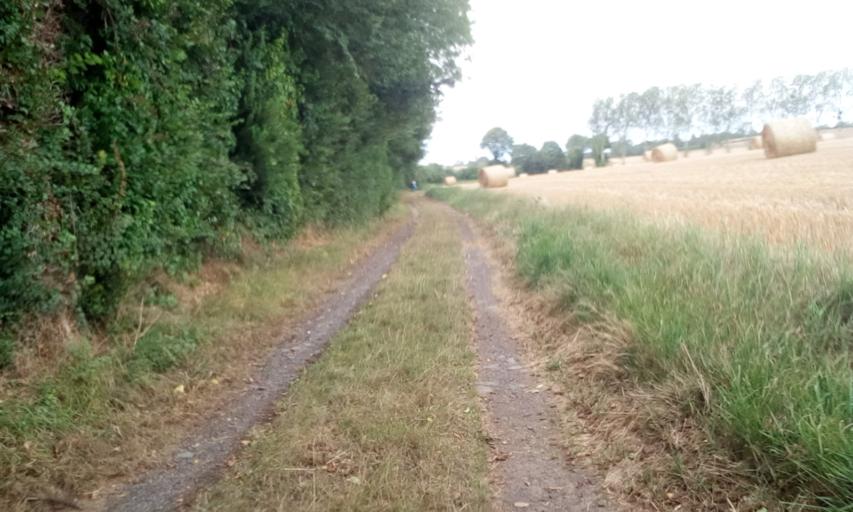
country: FR
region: Lower Normandy
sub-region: Departement du Calvados
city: Tilly-sur-Seulles
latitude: 49.2267
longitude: -0.6229
